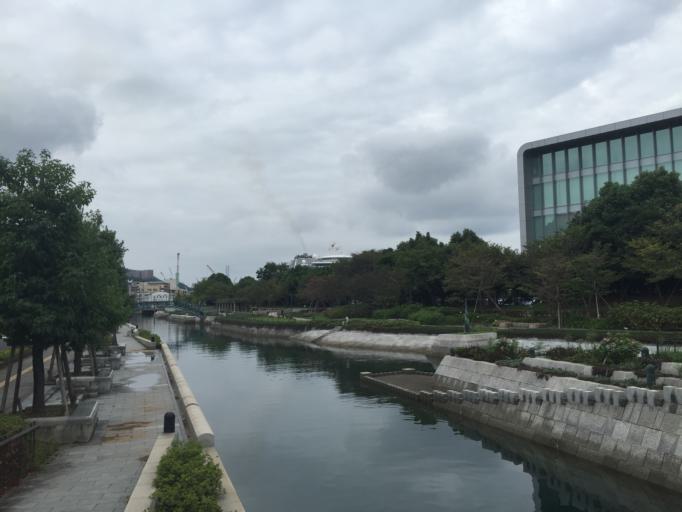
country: JP
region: Nagasaki
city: Nagasaki-shi
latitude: 32.7400
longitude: 129.8718
